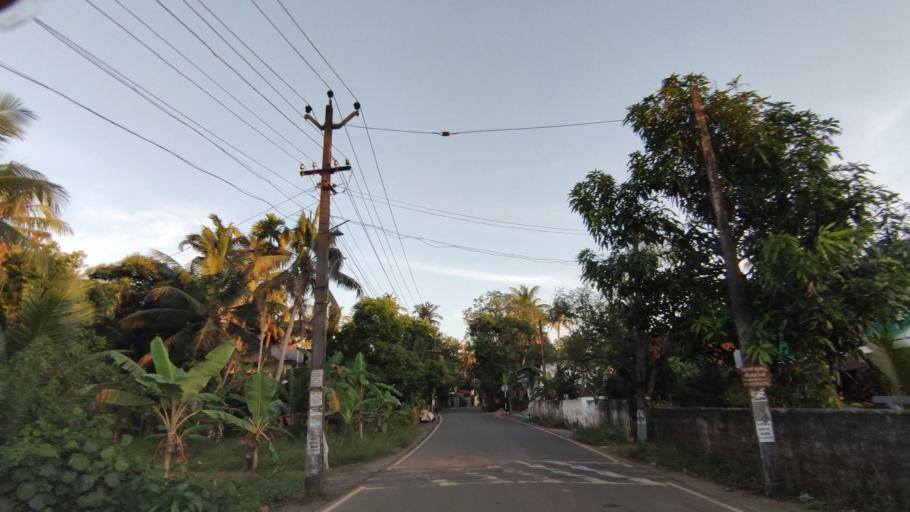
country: IN
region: Kerala
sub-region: Kottayam
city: Kottayam
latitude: 9.6289
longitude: 76.4850
